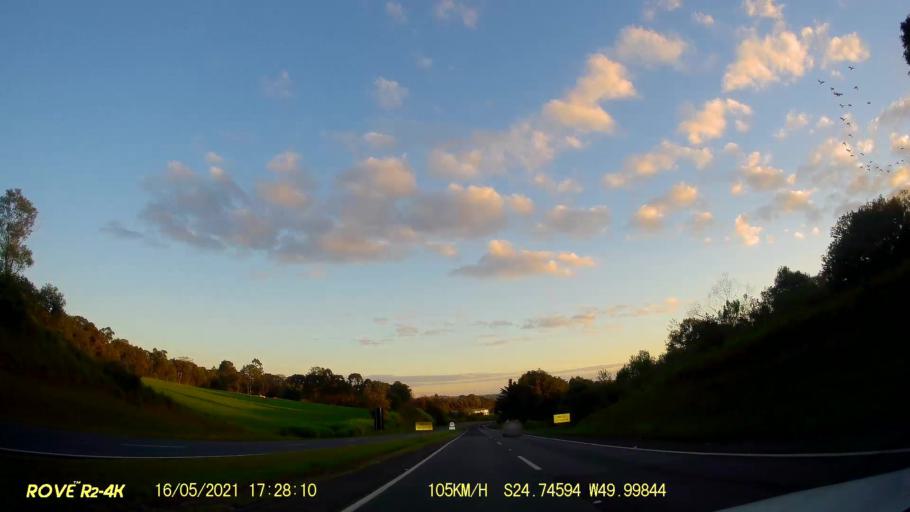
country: BR
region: Parana
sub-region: Castro
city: Castro
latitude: -24.7463
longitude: -49.9990
